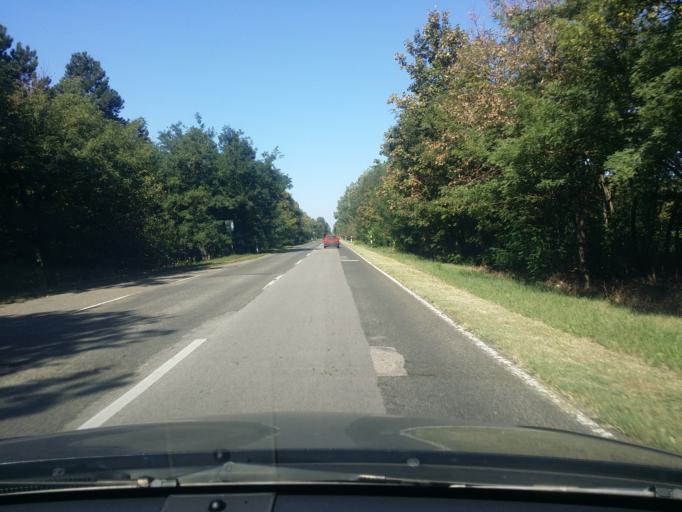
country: HU
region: Csongrad
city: Pusztaszer
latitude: 46.5447
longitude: 19.9536
